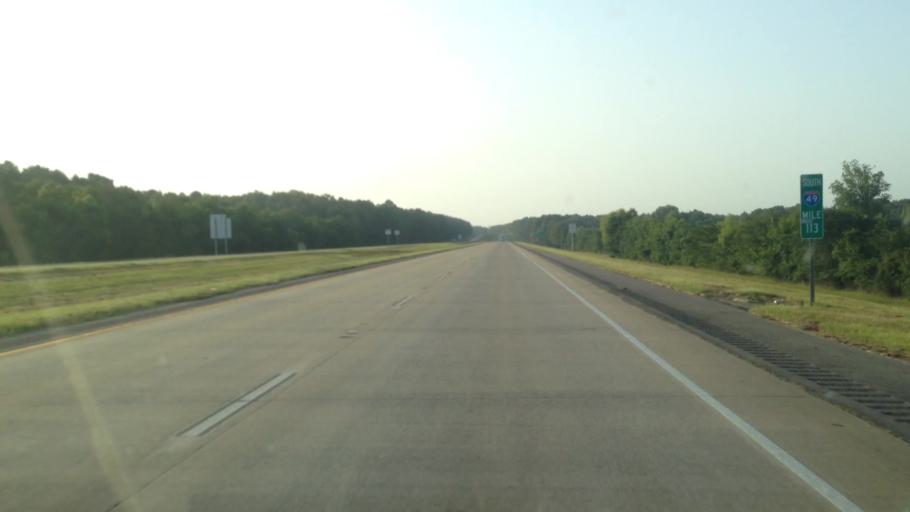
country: US
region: Louisiana
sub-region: Grant Parish
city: Colfax
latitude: 31.4862
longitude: -92.8506
